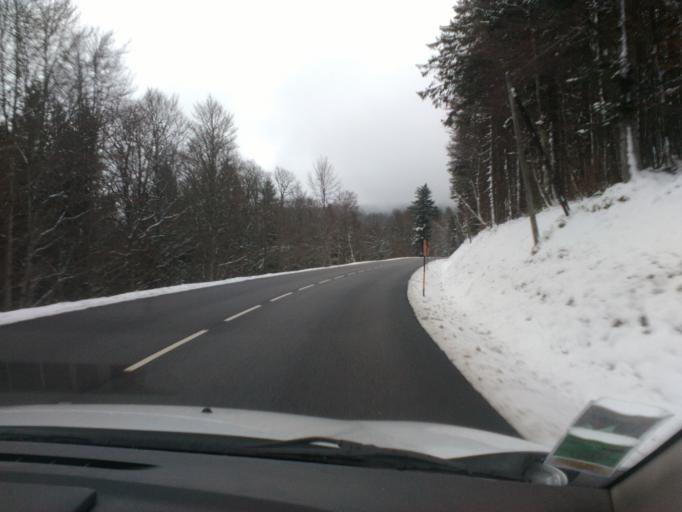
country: FR
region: Alsace
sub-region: Departement du Haut-Rhin
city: Metzeral
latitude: 48.0617
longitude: 7.0144
